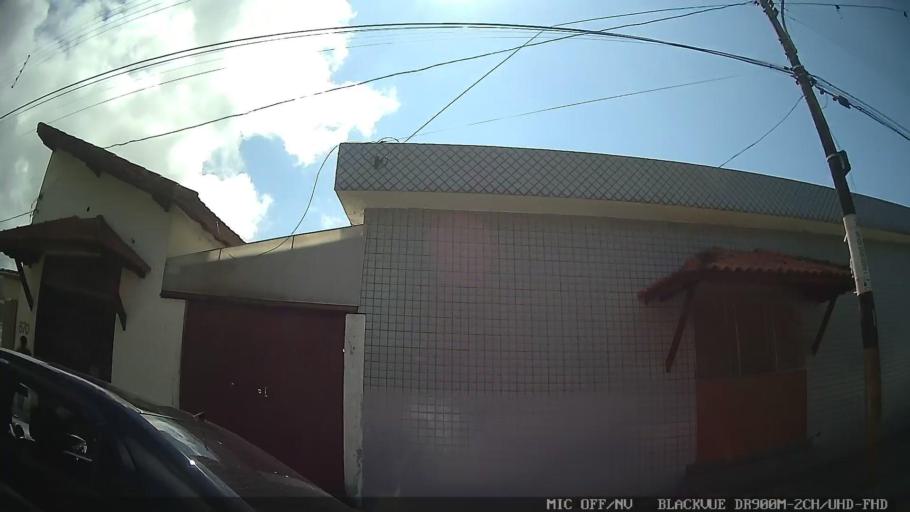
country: BR
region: Sao Paulo
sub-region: Peruibe
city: Peruibe
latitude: -24.3079
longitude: -47.0056
